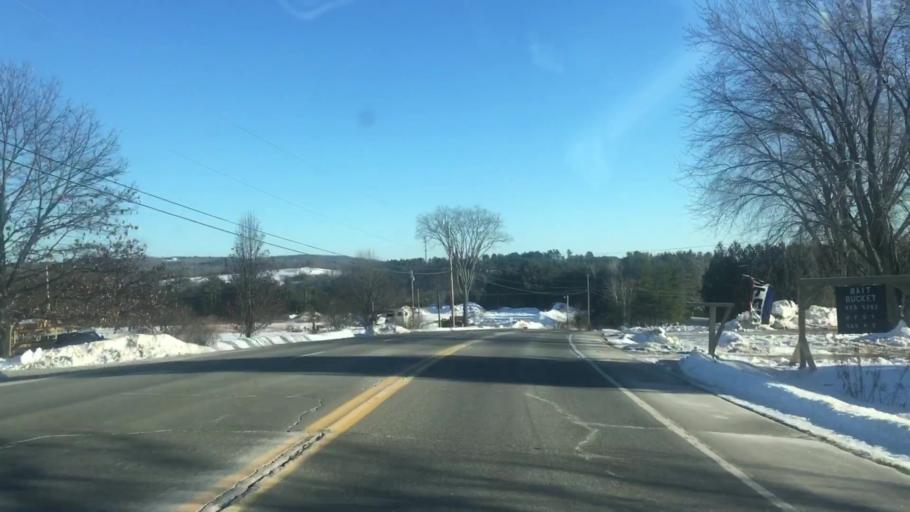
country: US
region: Maine
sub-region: Somerset County
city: Norridgewock
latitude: 44.7224
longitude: -69.8005
